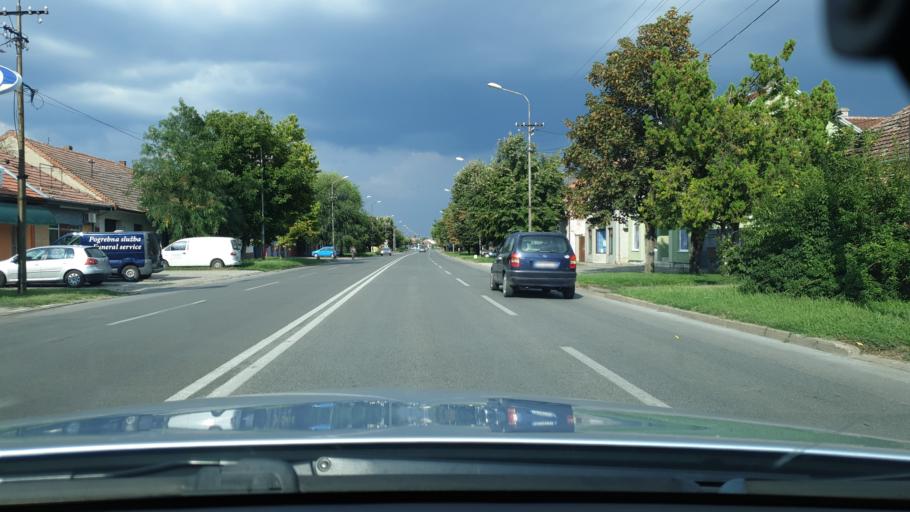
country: RS
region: Autonomna Pokrajina Vojvodina
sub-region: Srednjebanatski Okrug
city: Zrenjanin
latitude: 45.3806
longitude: 20.4019
